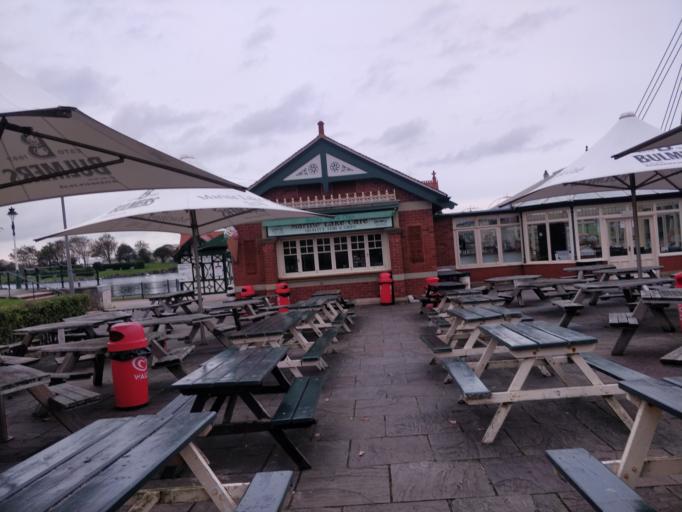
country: GB
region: England
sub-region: Sefton
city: Southport
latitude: 53.6504
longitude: -3.0086
